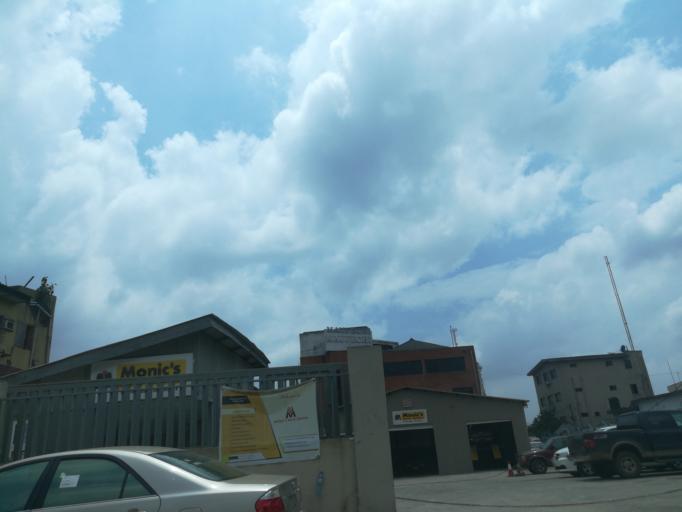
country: NG
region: Lagos
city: Ikeja
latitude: 6.5947
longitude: 3.3577
